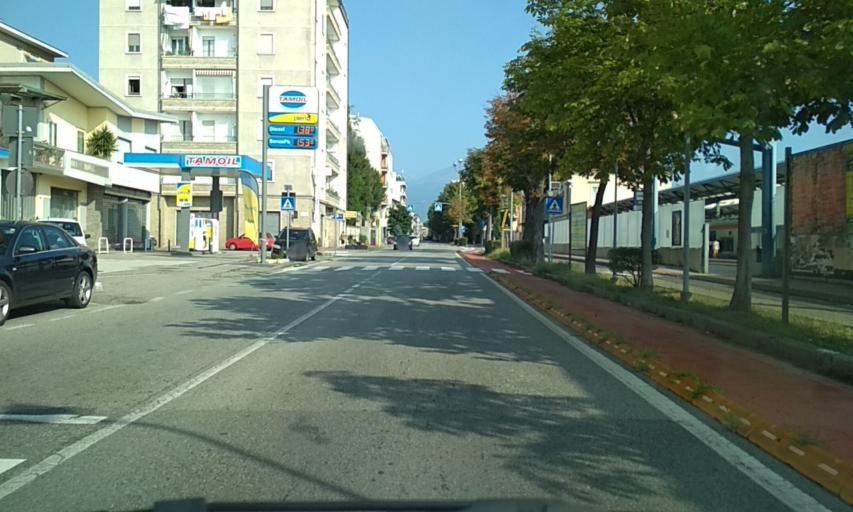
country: IT
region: Piedmont
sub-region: Provincia di Torino
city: Rivarolo Canavese
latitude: 45.3274
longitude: 7.7266
